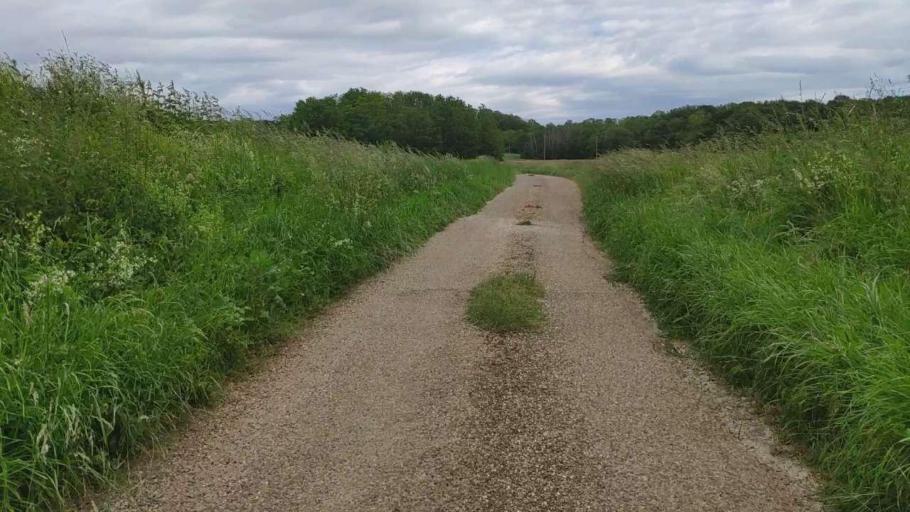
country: FR
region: Franche-Comte
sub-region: Departement du Jura
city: Bletterans
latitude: 46.7885
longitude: 5.5446
